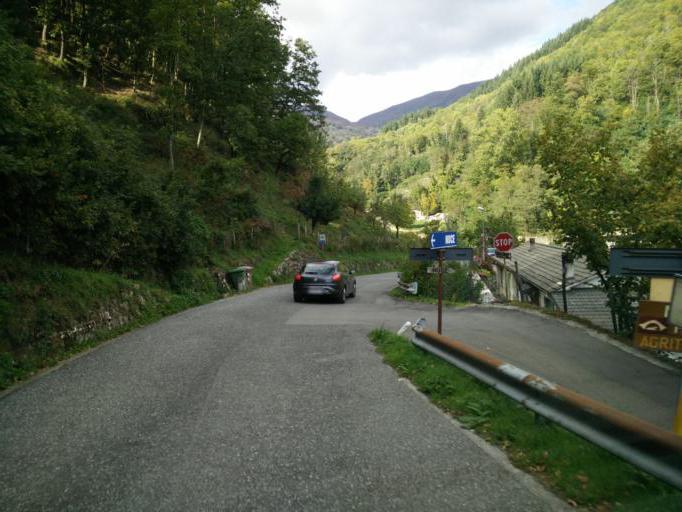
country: IT
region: Tuscany
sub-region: Provincia di Massa-Carrara
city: Patigno
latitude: 44.3506
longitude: 9.7710
